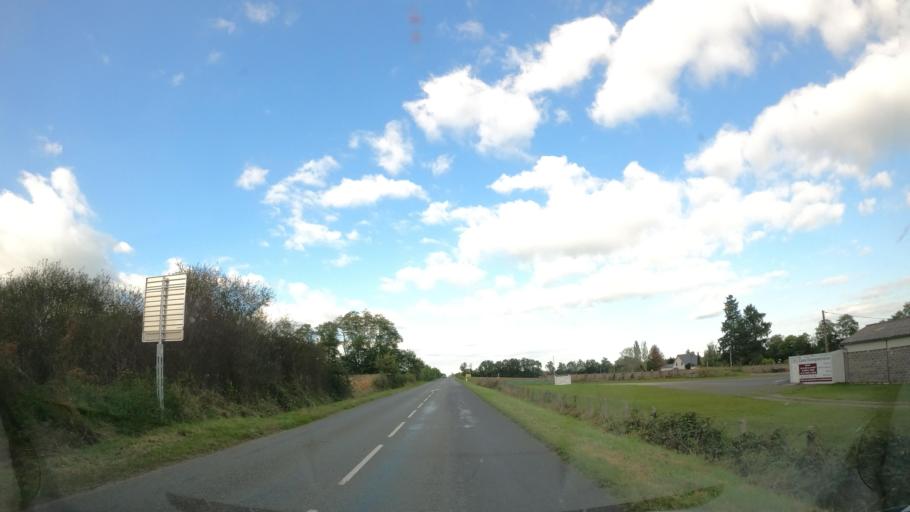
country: FR
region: Auvergne
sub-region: Departement de l'Allier
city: Dompierre-sur-Besbre
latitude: 46.5043
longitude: 3.6695
